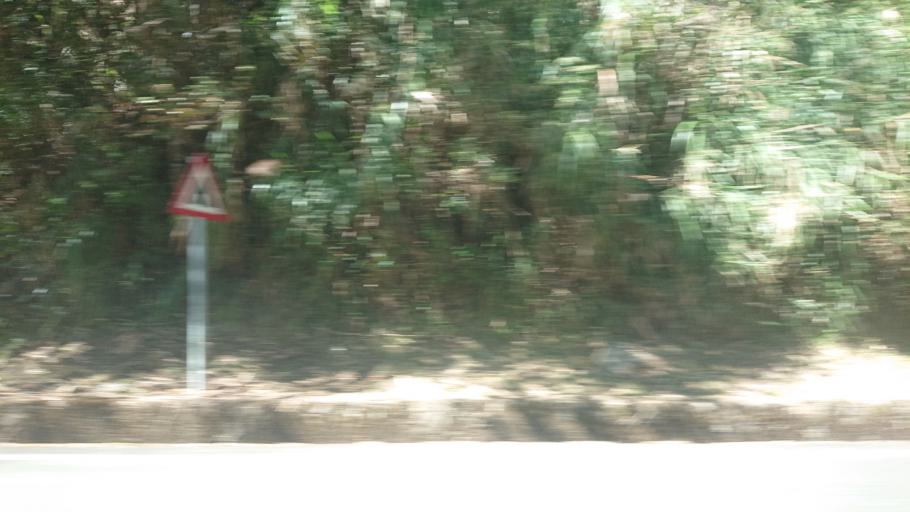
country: TW
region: Taiwan
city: Lugu
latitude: 23.4768
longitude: 120.8378
